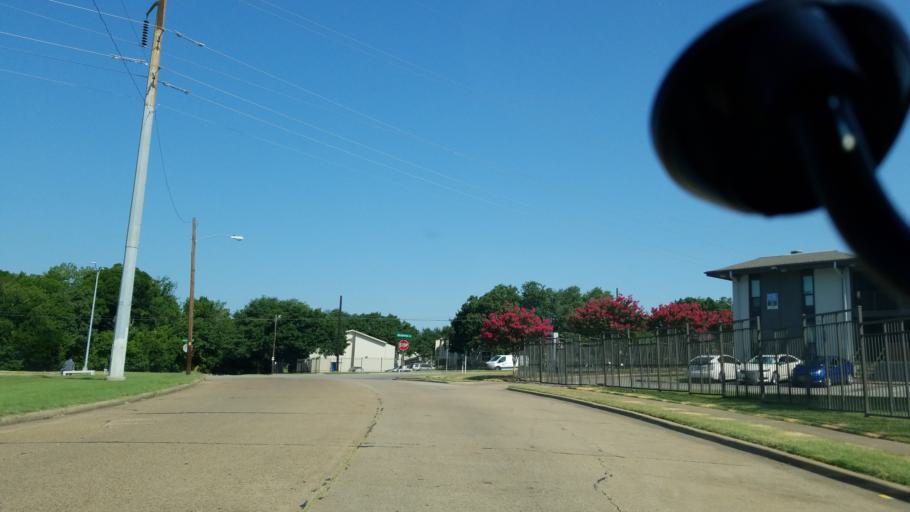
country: US
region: Texas
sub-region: Dallas County
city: Cockrell Hill
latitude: 32.7067
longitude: -96.8737
